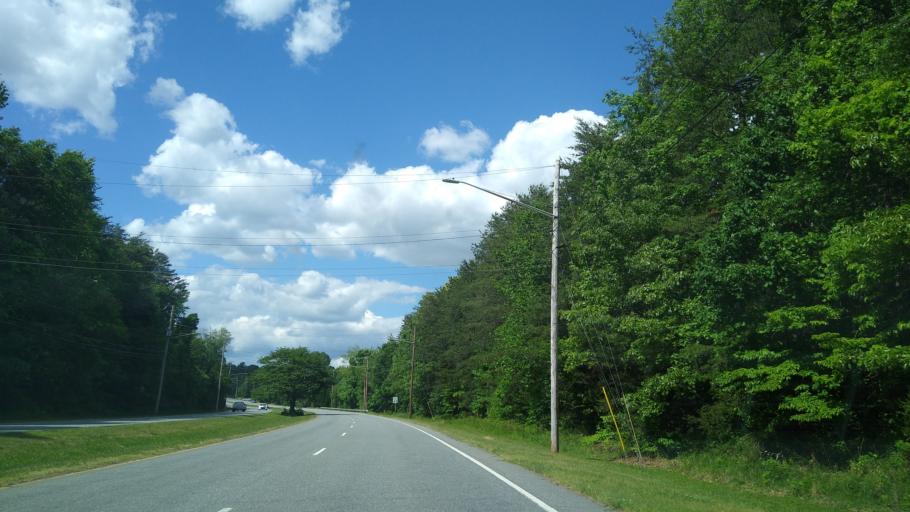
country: US
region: North Carolina
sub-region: Guilford County
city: High Point
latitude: 35.9968
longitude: -80.0085
